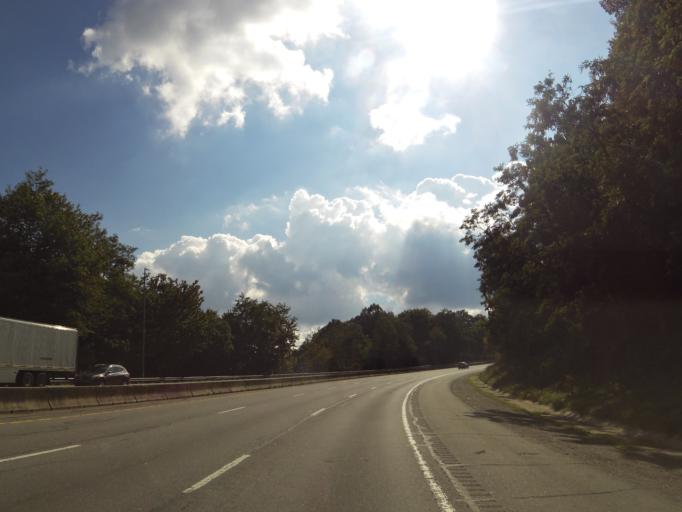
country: US
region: North Carolina
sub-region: Buncombe County
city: Black Mountain
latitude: 35.6234
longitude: -82.2191
